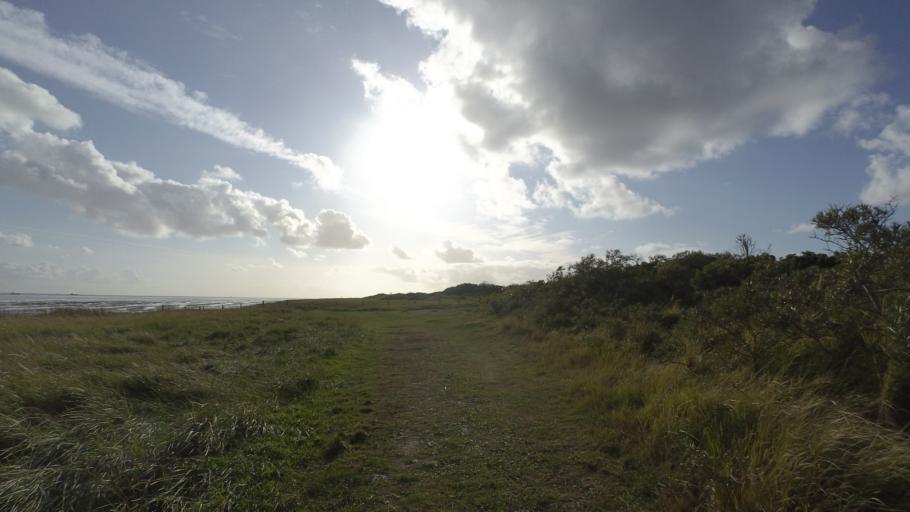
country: NL
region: Friesland
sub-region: Gemeente Dongeradeel
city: Holwerd
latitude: 53.4564
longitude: 5.9031
